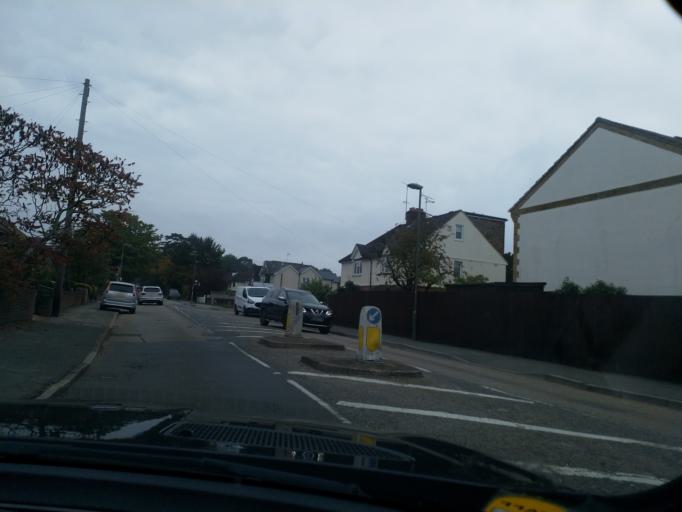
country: GB
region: England
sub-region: Surrey
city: Frimley
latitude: 51.3256
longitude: -0.7528
